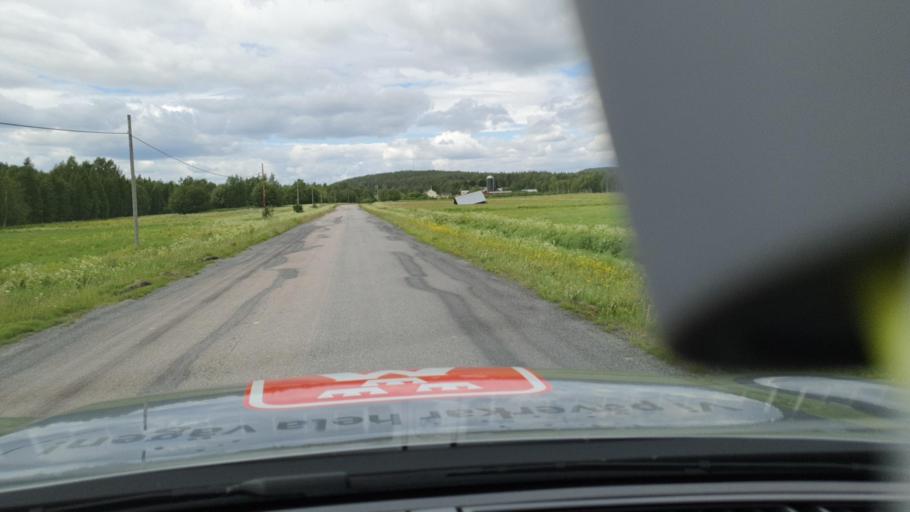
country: SE
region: Norrbotten
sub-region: Bodens Kommun
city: Saevast
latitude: 65.8650
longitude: 21.9044
